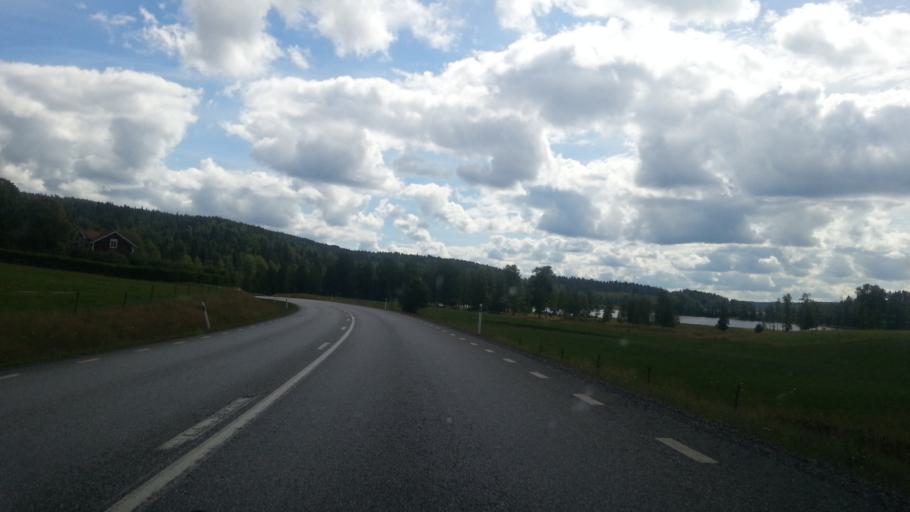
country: SE
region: OErebro
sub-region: Ljusnarsbergs Kommun
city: Kopparberg
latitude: 59.8350
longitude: 15.0997
